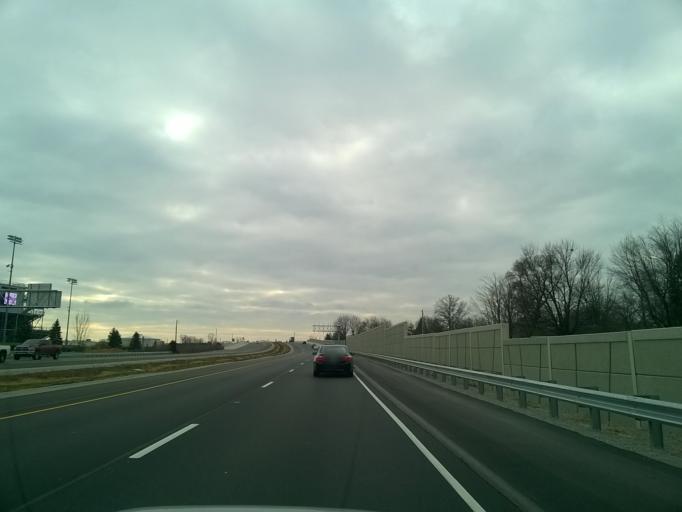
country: US
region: Indiana
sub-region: Hamilton County
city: Westfield
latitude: 40.0533
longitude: -86.1330
